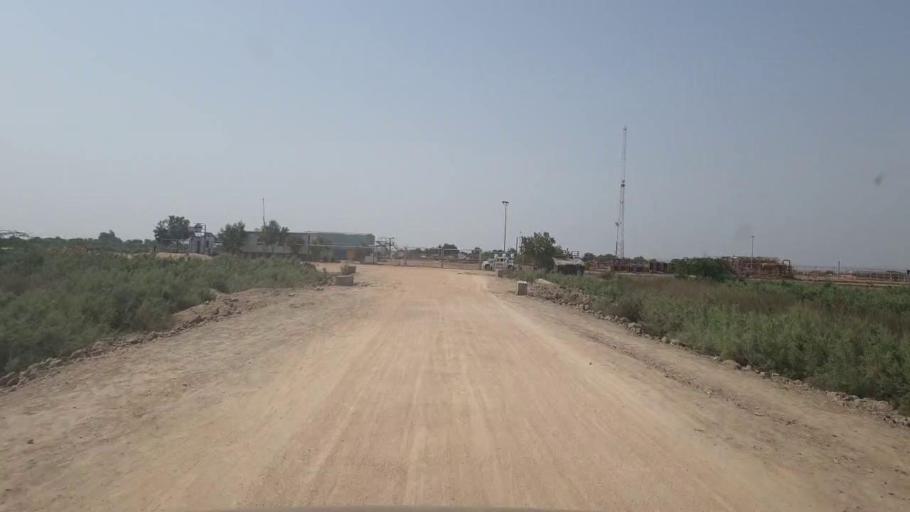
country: PK
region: Sindh
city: Jati
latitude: 24.3603
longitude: 68.5557
